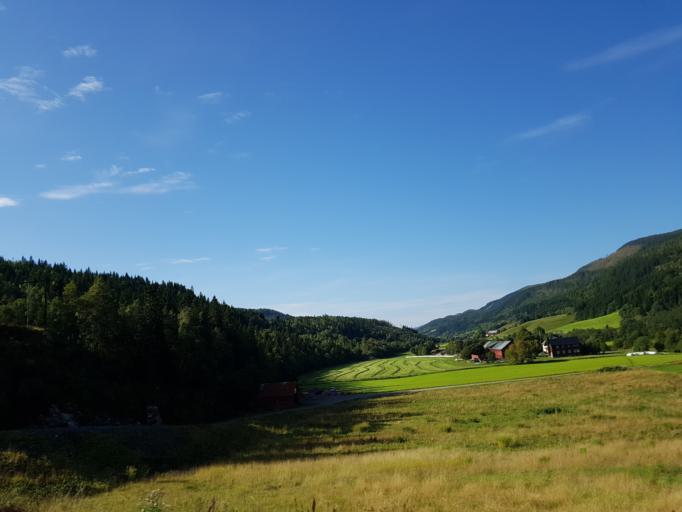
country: NO
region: Sor-Trondelag
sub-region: Rissa
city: Rissa
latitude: 63.6707
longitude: 10.2137
